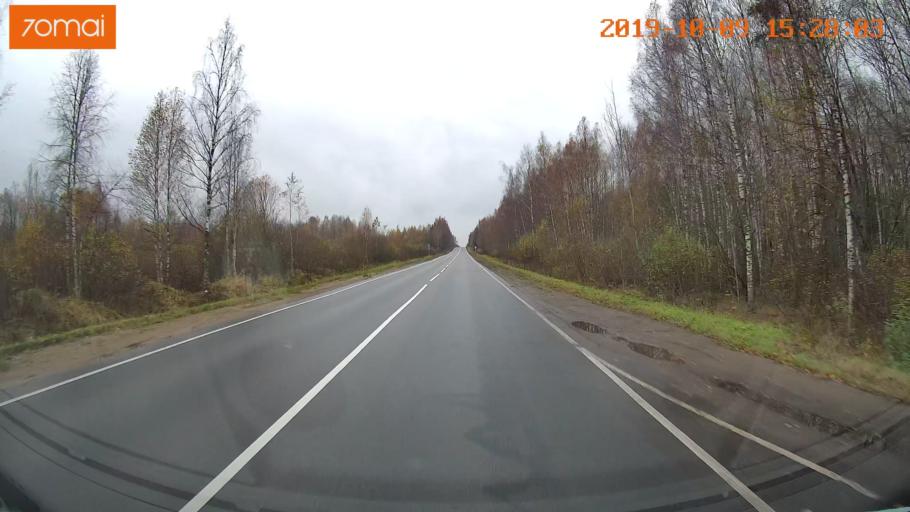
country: RU
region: Kostroma
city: Susanino
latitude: 58.0076
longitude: 41.3666
